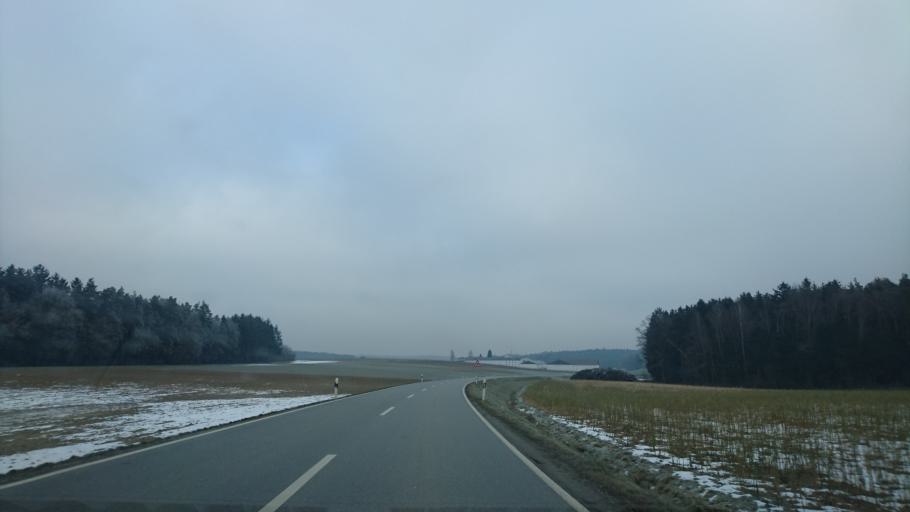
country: DE
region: Bavaria
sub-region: Lower Bavaria
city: Ruhstorf
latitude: 48.5607
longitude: 12.6707
